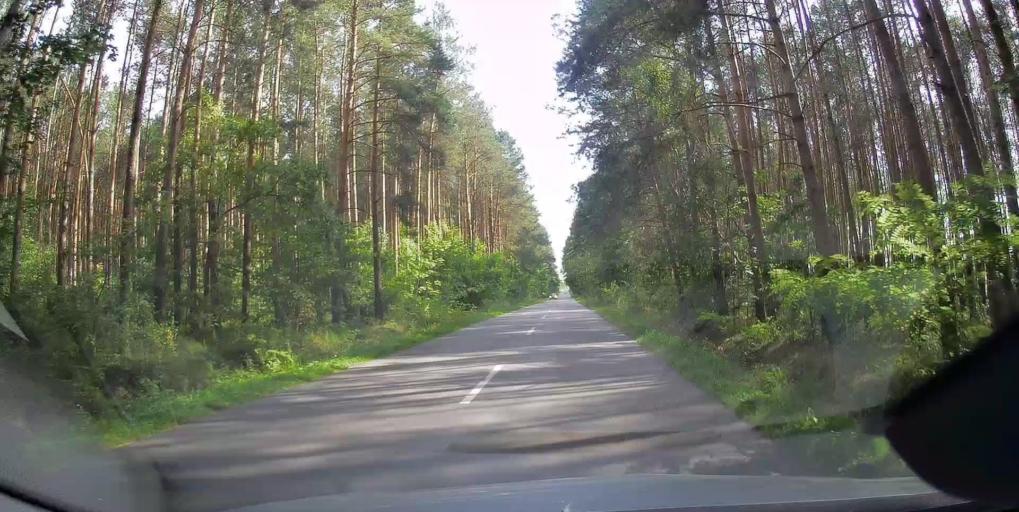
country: PL
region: Lodz Voivodeship
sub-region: Powiat opoczynski
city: Mniszkow
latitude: 51.3946
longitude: 20.0365
